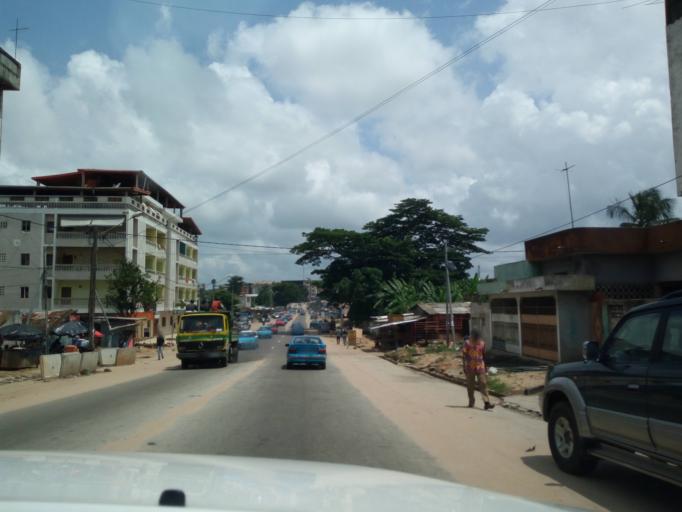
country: CI
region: Lagunes
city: Abidjan
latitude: 5.3395
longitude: -4.0931
